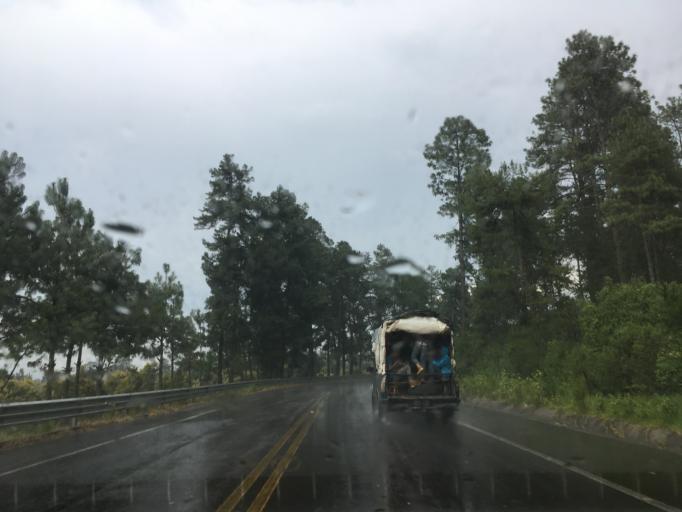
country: MX
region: Michoacan
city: Angahuan
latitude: 19.5701
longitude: -102.2745
